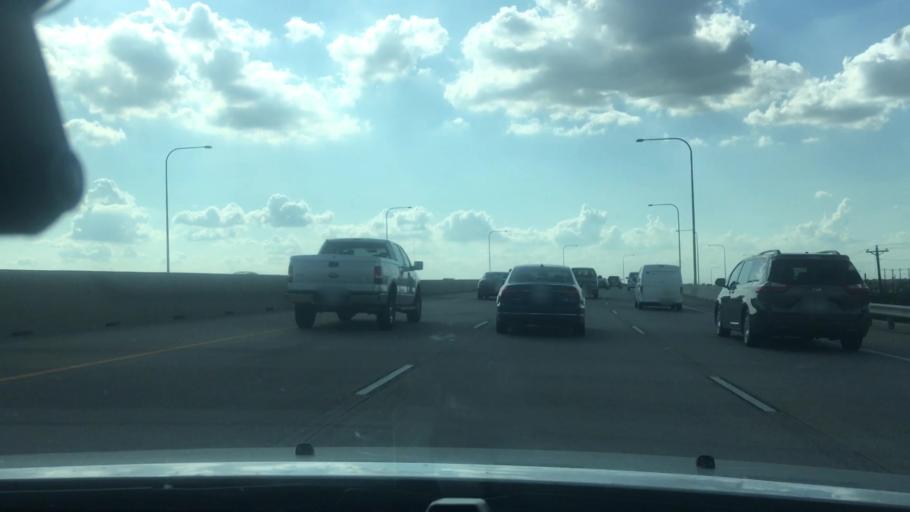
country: US
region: Texas
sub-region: Collin County
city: Frisco
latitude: 33.1368
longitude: -96.8340
